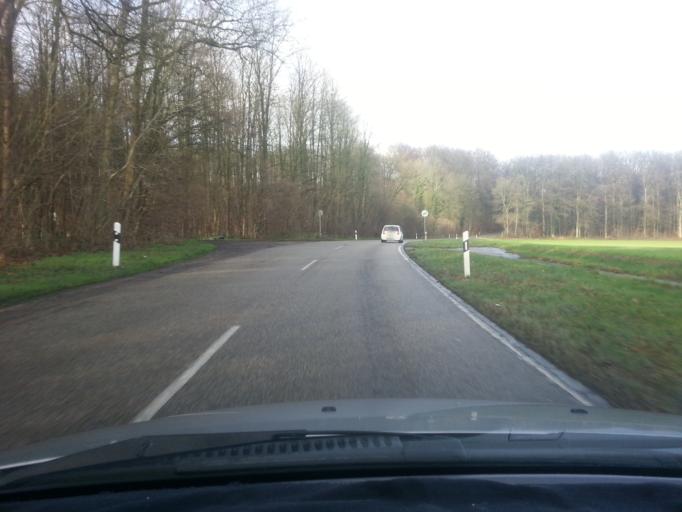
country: DE
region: Baden-Wuerttemberg
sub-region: Karlsruhe Region
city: Zaisenhausen
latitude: 49.1855
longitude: 8.8320
